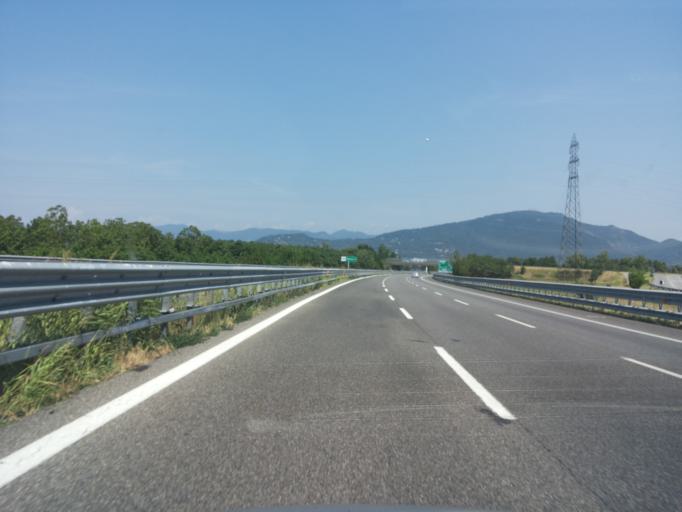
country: IT
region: Lombardy
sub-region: Provincia di Brescia
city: San Zeno Naviglio
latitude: 45.4941
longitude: 10.2287
